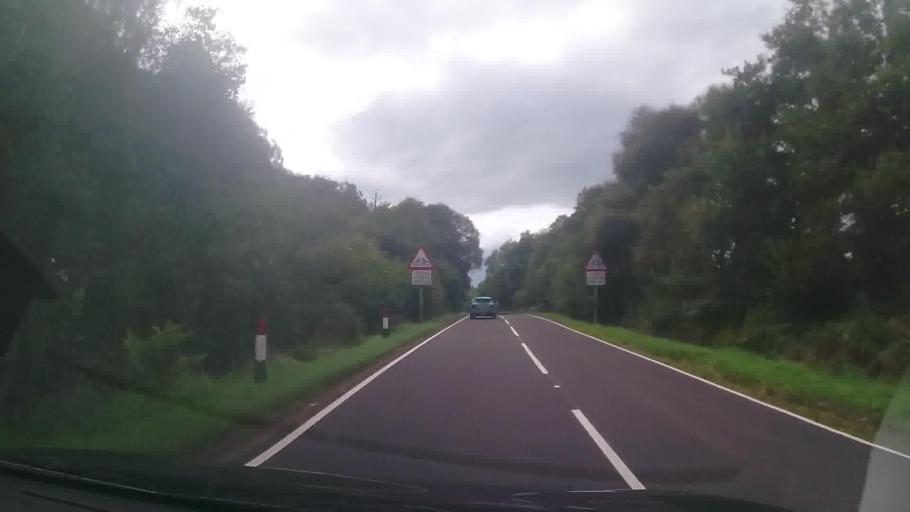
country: GB
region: Scotland
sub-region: Argyll and Bute
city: Oban
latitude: 56.6220
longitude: -5.3196
